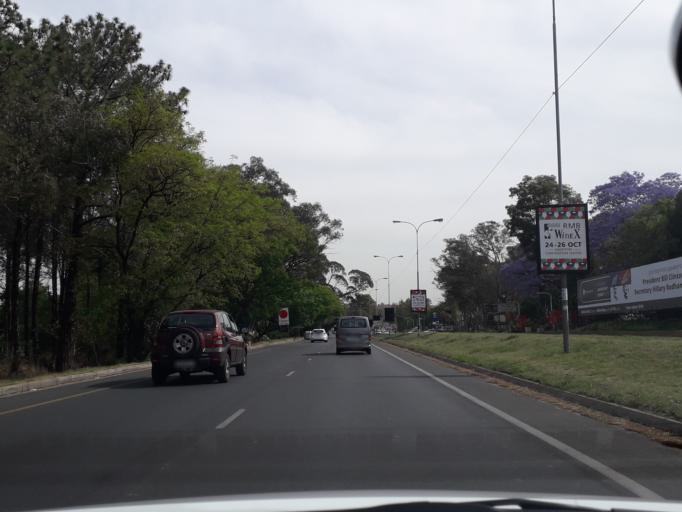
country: ZA
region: Gauteng
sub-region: City of Johannesburg Metropolitan Municipality
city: Diepsloot
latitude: -26.0296
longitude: 28.0282
